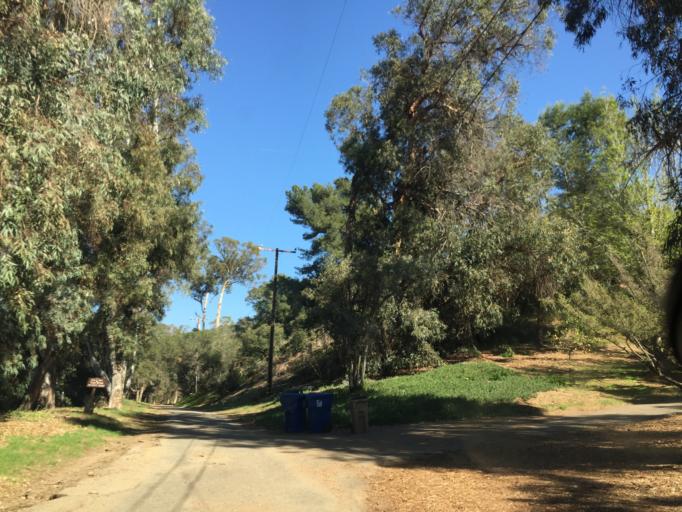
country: US
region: California
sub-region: Santa Barbara County
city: Mission Canyon
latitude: 34.4351
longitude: -119.7688
